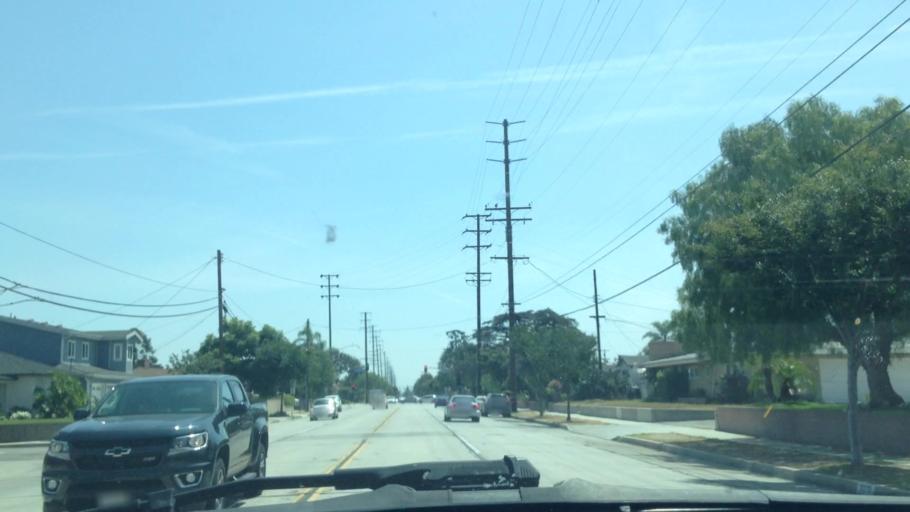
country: US
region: California
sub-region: Los Angeles County
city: Downey
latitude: 33.9229
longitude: -118.1457
